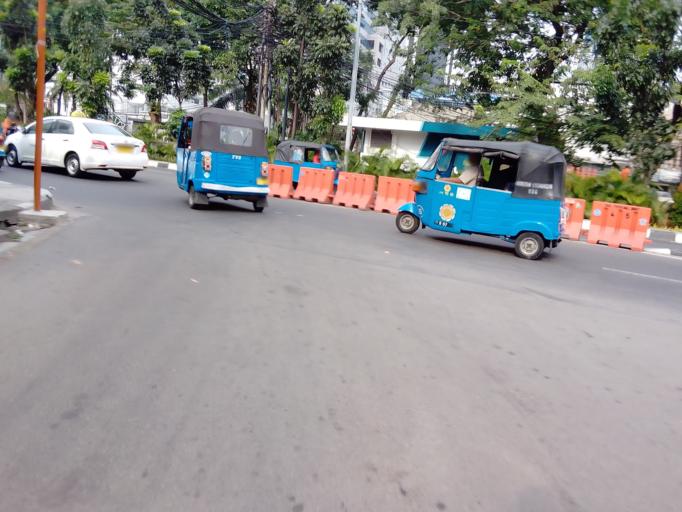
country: ID
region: Jakarta Raya
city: Jakarta
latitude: -6.1794
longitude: 106.8181
